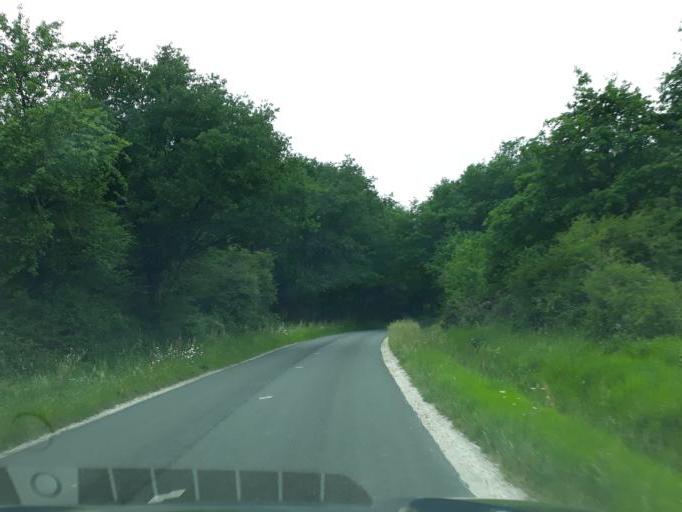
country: FR
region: Centre
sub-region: Departement du Loiret
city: Saint-Pere-sur-Loire
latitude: 47.7251
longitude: 2.3190
